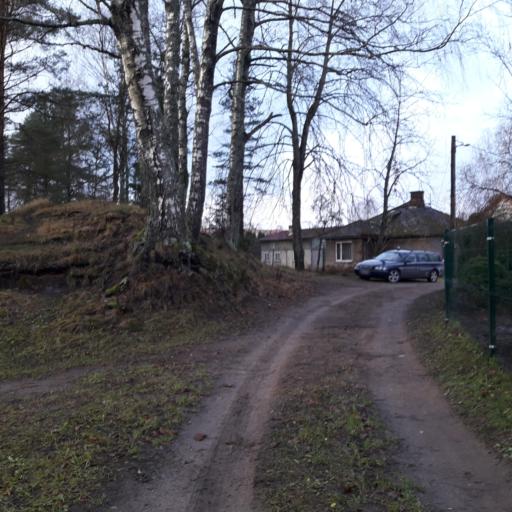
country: LV
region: Valmieras Rajons
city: Valmiera
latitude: 57.5349
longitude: 25.4333
